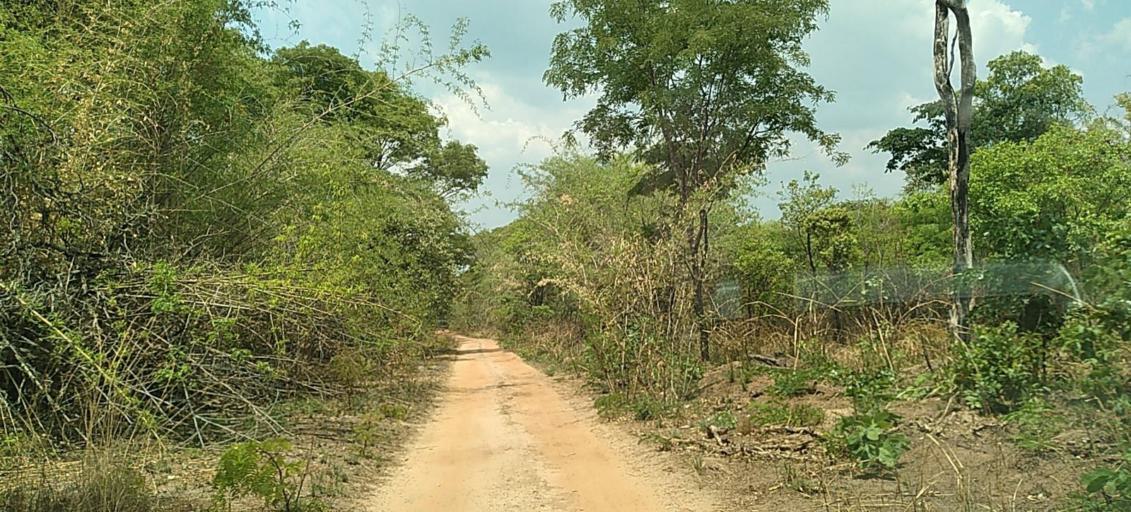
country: ZM
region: Copperbelt
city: Chingola
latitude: -12.7695
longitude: 27.6983
